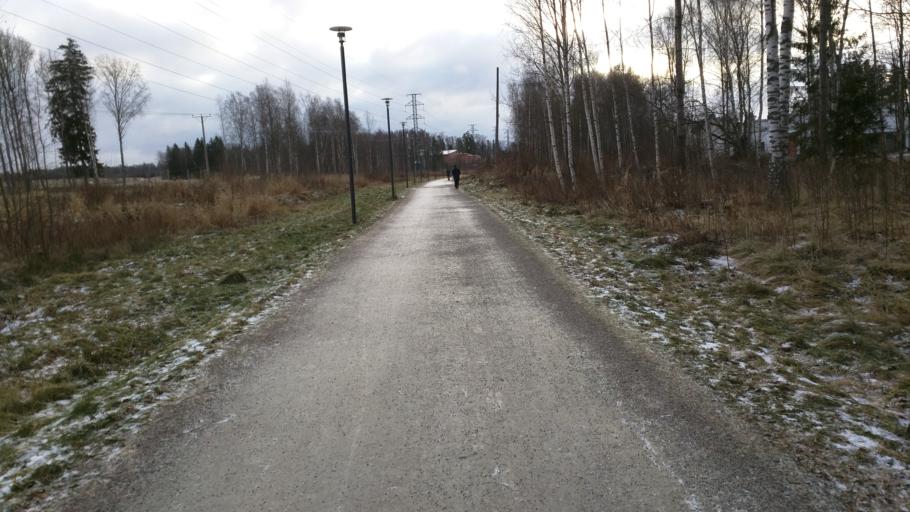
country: FI
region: Uusimaa
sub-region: Helsinki
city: Kilo
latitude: 60.1976
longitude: 24.7743
